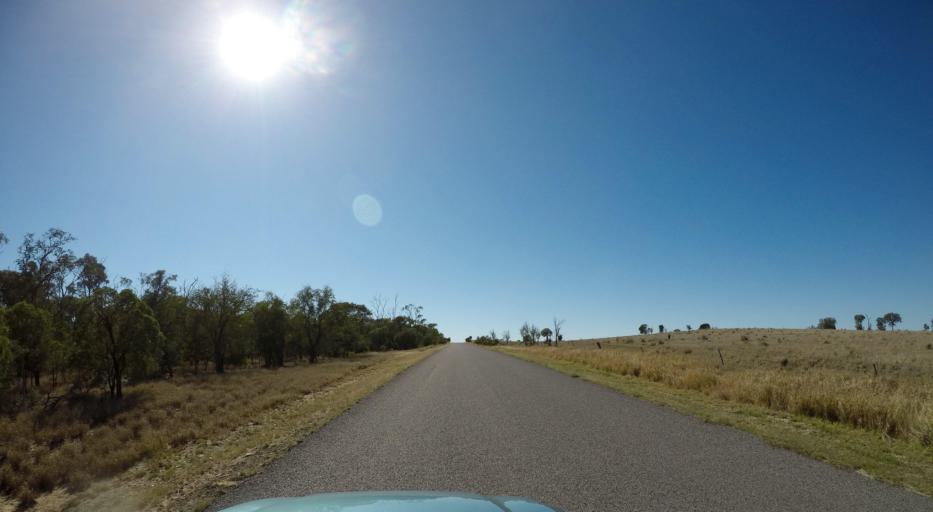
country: AU
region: Queensland
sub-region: Banana
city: Taroom
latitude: -25.7886
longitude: 149.6847
